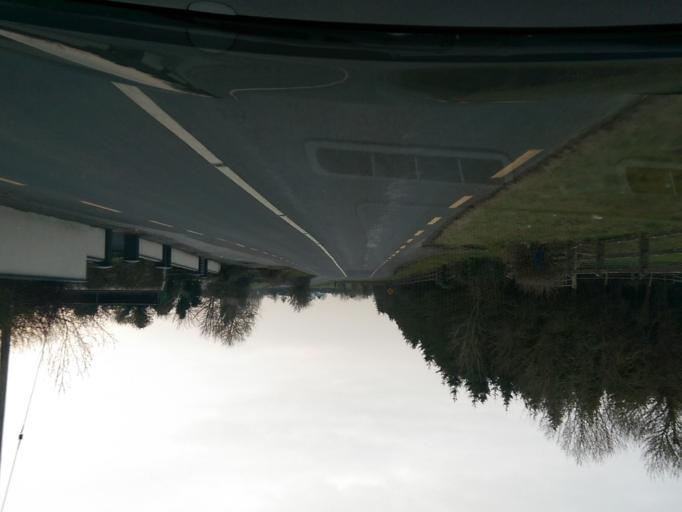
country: IE
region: Leinster
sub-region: An Longfort
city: Ballymahon
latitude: 53.5121
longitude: -7.8246
